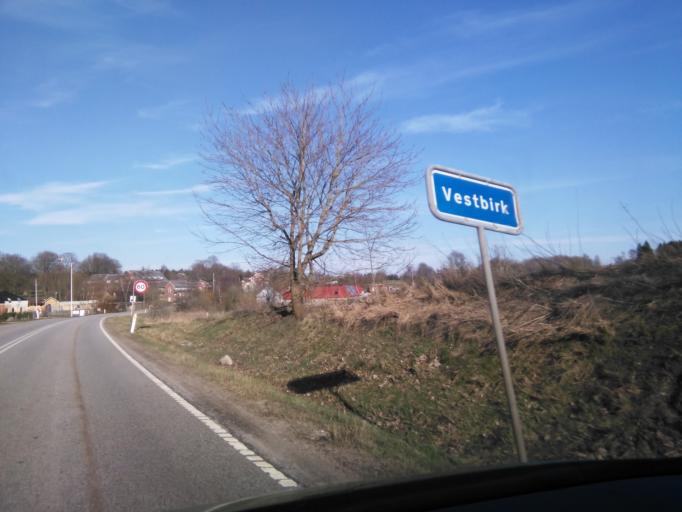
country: DK
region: Central Jutland
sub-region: Horsens Kommune
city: Braedstrup
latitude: 55.9644
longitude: 9.7154
